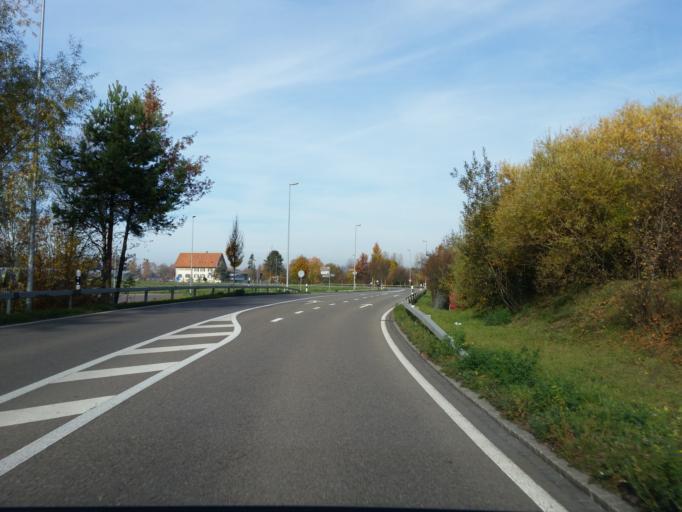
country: CH
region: Thurgau
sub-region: Kreuzlingen District
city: Gottlieben
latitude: 47.6583
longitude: 9.1465
